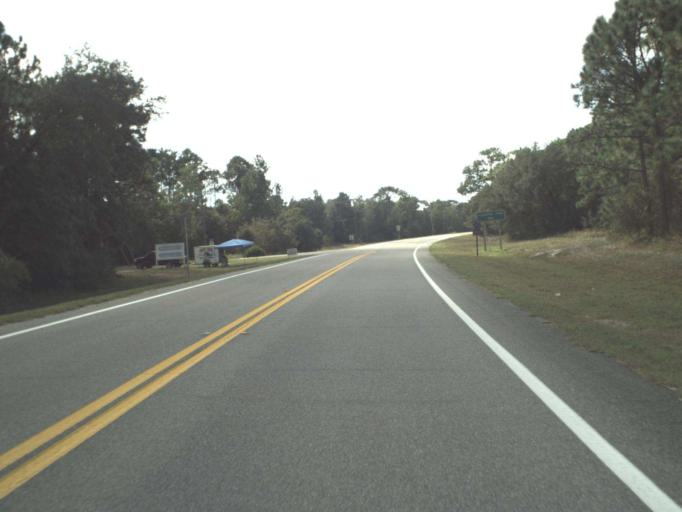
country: US
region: Florida
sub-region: Wakulla County
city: Crawfordville
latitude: 29.9439
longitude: -84.3867
